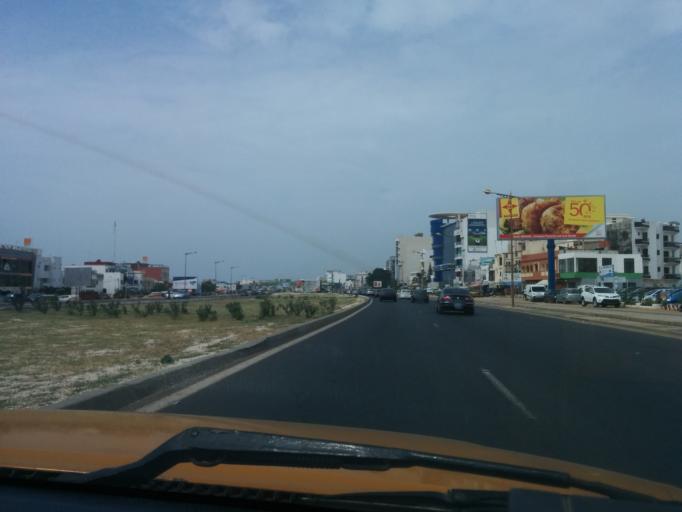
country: SN
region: Dakar
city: Mermoz Boabab
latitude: 14.7231
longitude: -17.4709
